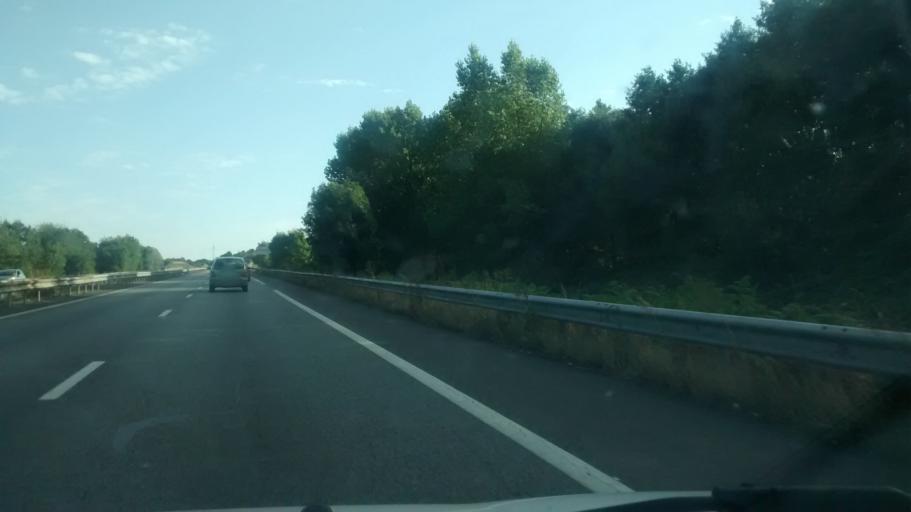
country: FR
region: Brittany
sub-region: Departement d'Ille-et-Vilaine
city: Laille
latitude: 47.9862
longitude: -1.6957
